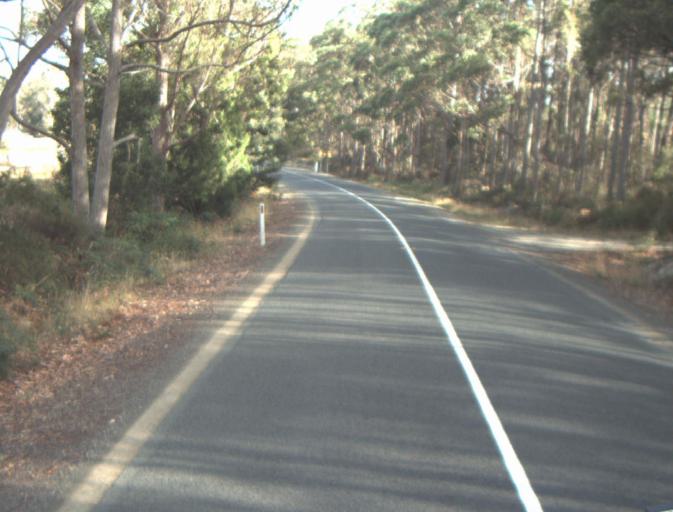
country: AU
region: Tasmania
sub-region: Dorset
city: Bridport
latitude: -41.1484
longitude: 147.2333
